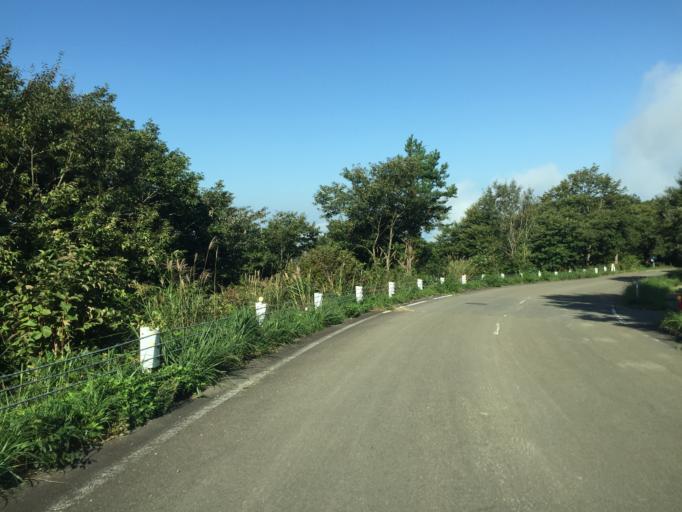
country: JP
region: Fukushima
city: Inawashiro
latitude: 37.4768
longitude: 139.9804
